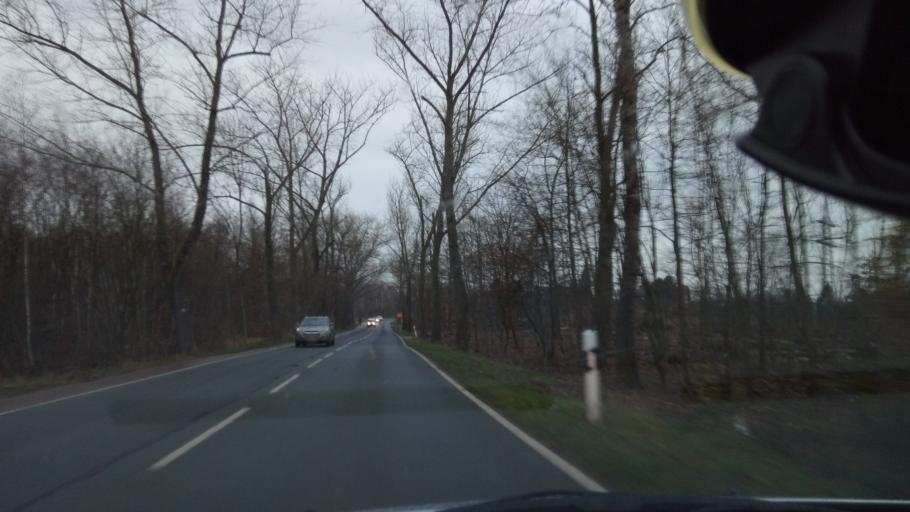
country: DE
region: Saxony-Anhalt
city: Muldenstein
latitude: 51.6597
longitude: 12.3504
